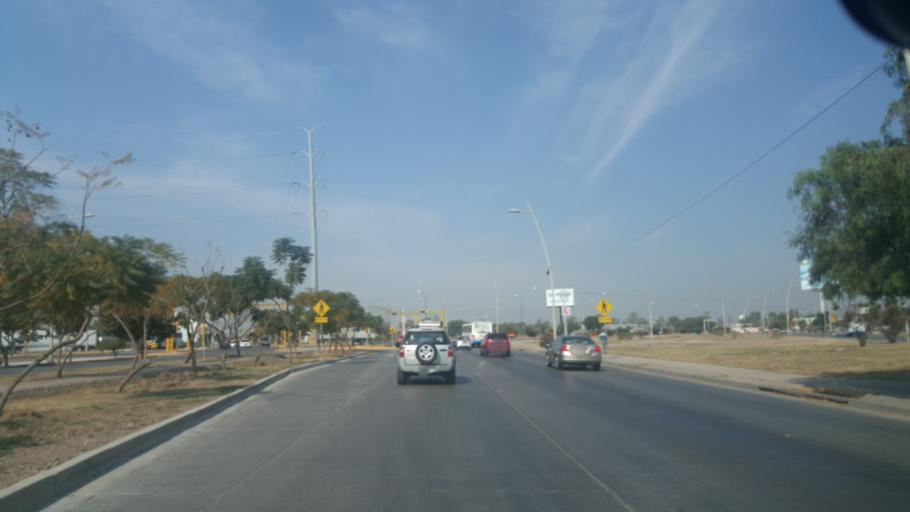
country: MX
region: Guanajuato
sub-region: Leon
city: Medina
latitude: 21.1409
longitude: -101.6315
